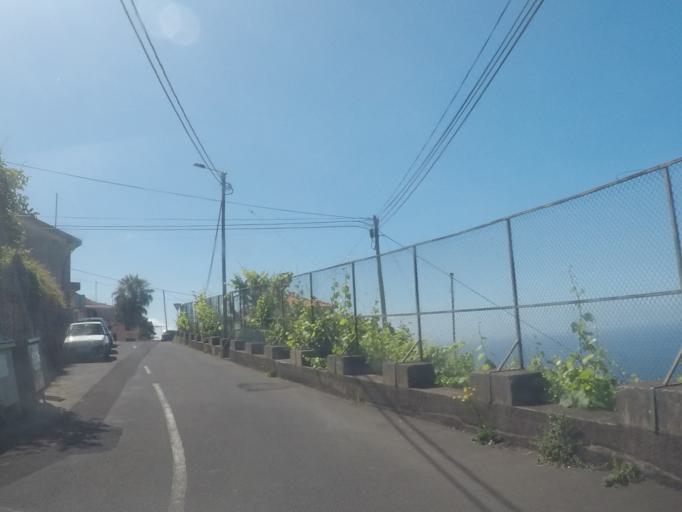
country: PT
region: Madeira
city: Camara de Lobos
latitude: 32.6695
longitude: -16.9659
